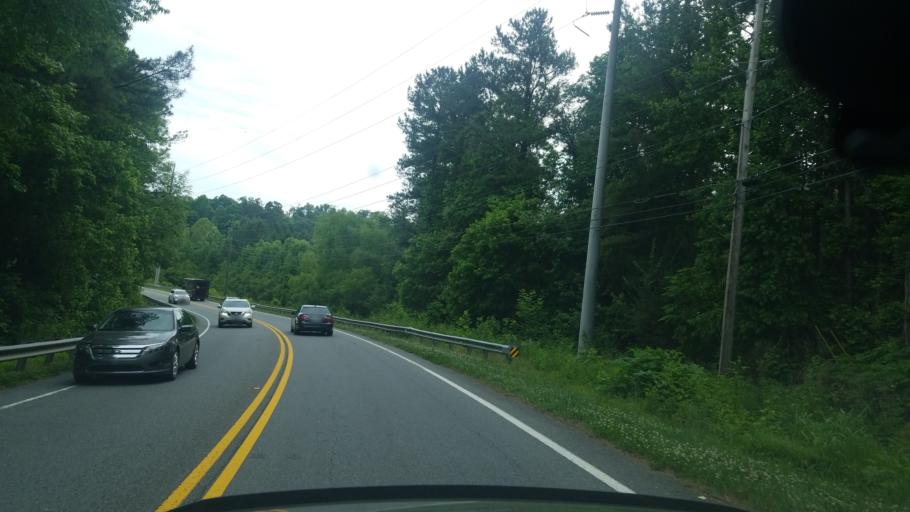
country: US
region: Georgia
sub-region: Gwinnett County
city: Suwanee
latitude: 34.0690
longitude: -84.1324
